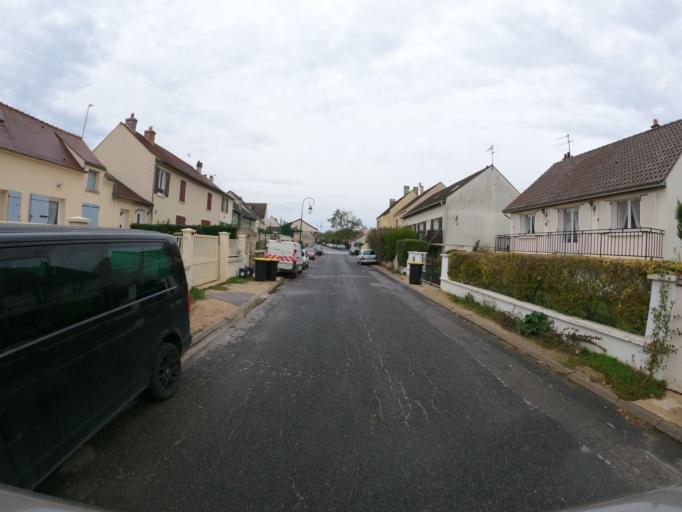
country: FR
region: Ile-de-France
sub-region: Departement de Seine-et-Marne
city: Villeneuve-le-Comte
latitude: 48.8161
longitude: 2.8314
